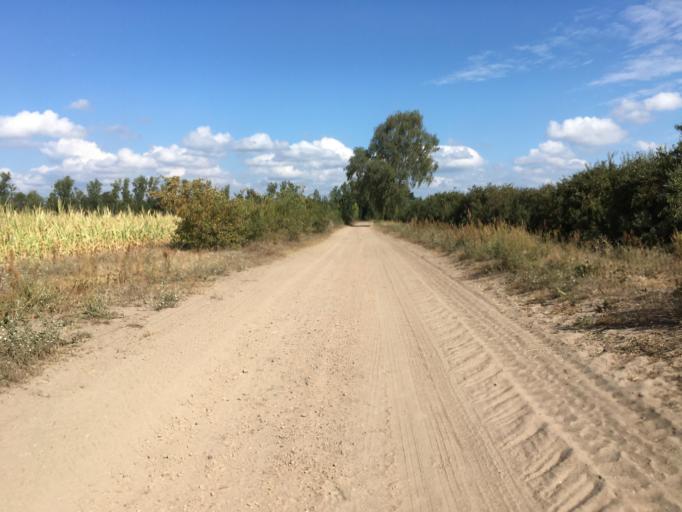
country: DE
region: Brandenburg
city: Zehdenick
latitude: 52.9773
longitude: 13.3813
